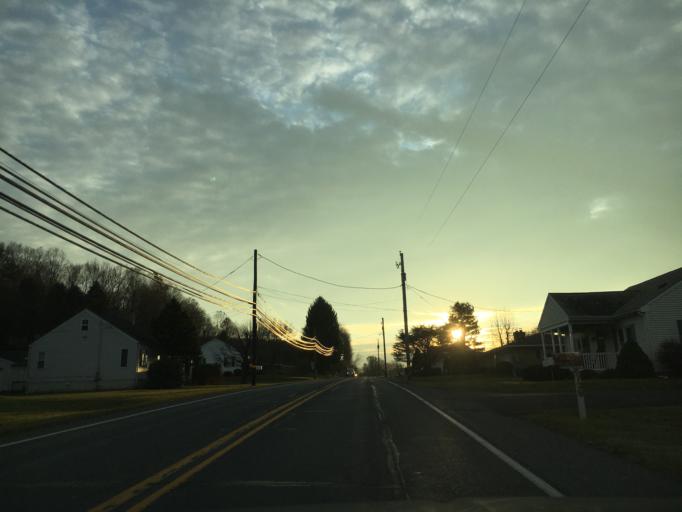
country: US
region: Pennsylvania
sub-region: Lehigh County
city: Slatington
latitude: 40.7223
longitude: -75.6184
